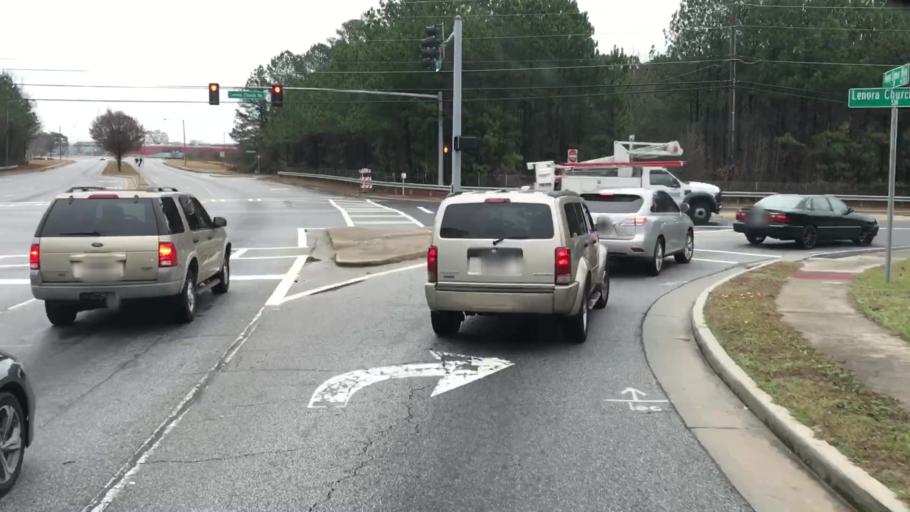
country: US
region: Georgia
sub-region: Gwinnett County
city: Snellville
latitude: 33.8526
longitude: -84.0194
